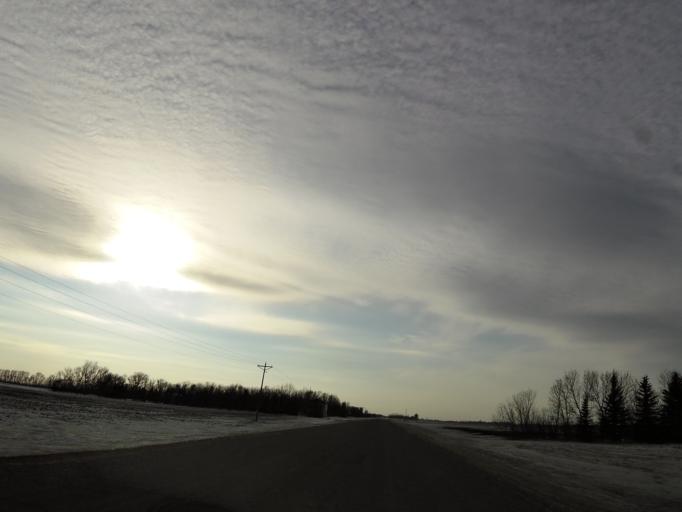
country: US
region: North Dakota
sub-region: Walsh County
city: Grafton
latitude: 48.4269
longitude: -97.3255
